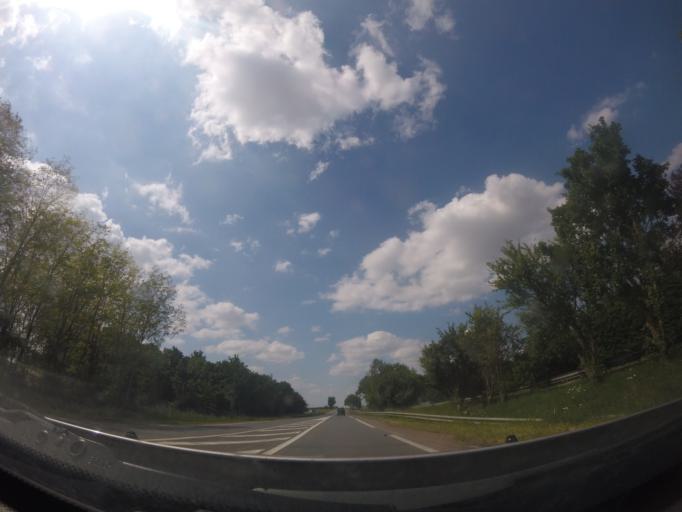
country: FR
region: Poitou-Charentes
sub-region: Departement de la Charente-Maritime
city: Saint-Porchaire
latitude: 45.8318
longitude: -0.8001
